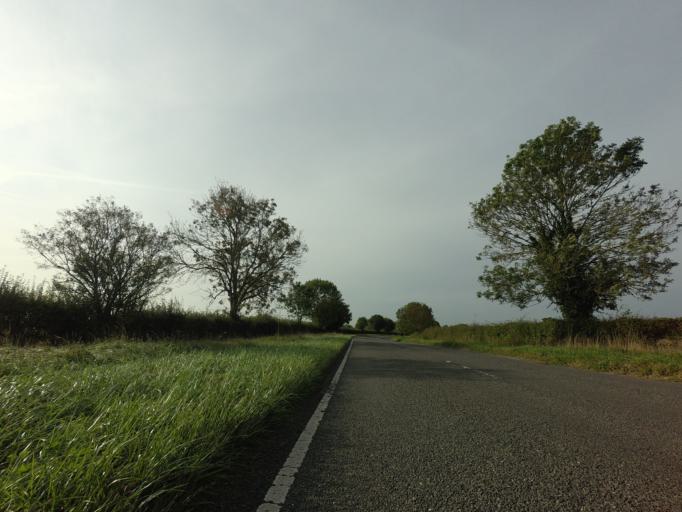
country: GB
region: England
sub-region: Cambridgeshire
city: Harston
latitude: 52.0985
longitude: 0.0822
